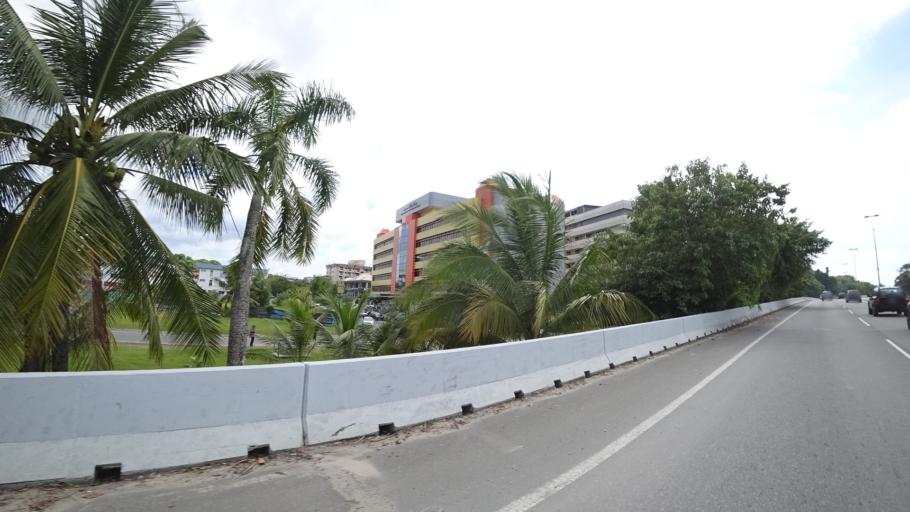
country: BN
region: Brunei and Muara
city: Bandar Seri Begawan
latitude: 4.8886
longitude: 114.9326
